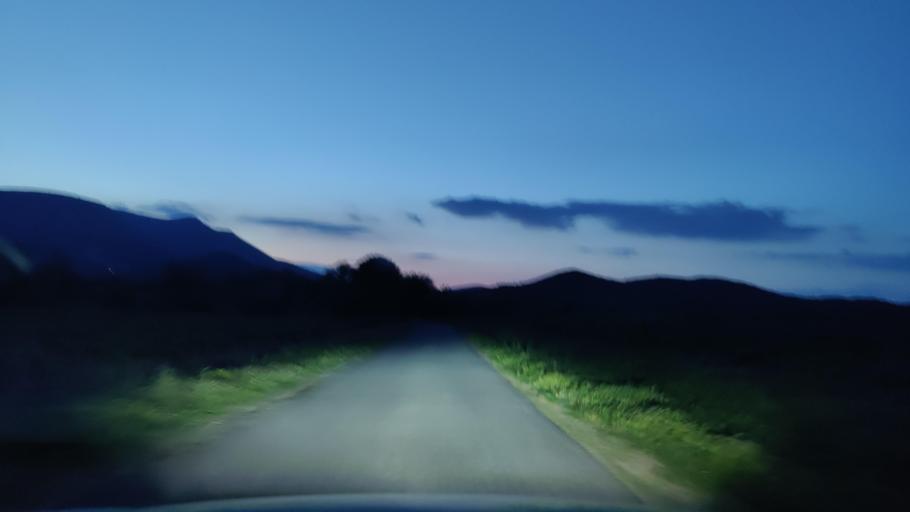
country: FR
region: Languedoc-Roussillon
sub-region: Departement des Pyrenees-Orientales
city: Estagel
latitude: 42.8836
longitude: 2.7357
